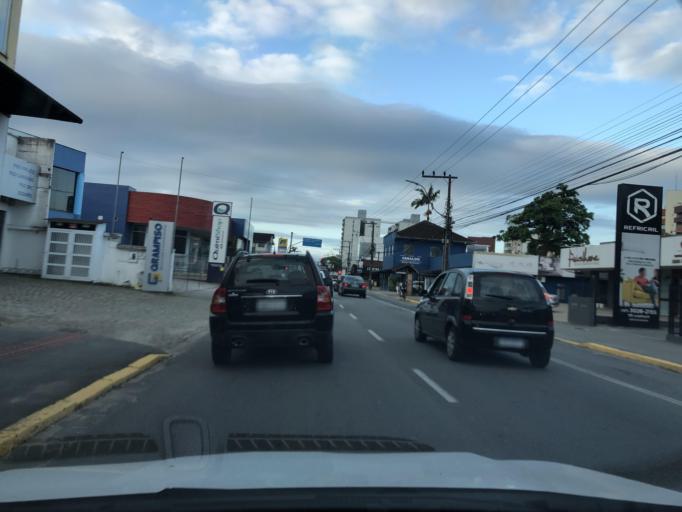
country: BR
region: Santa Catarina
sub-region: Joinville
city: Joinville
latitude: -26.2856
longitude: -48.8490
